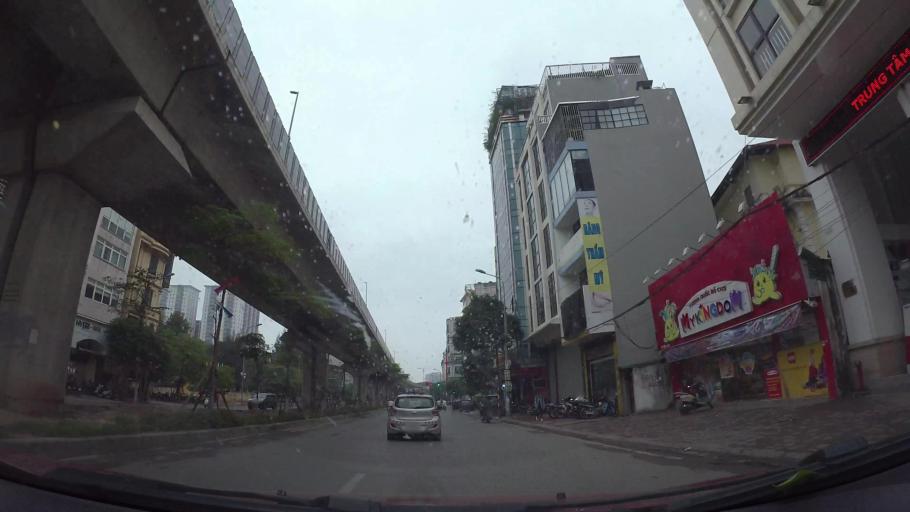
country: VN
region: Ha Noi
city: Dong Da
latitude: 21.0111
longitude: 105.8167
